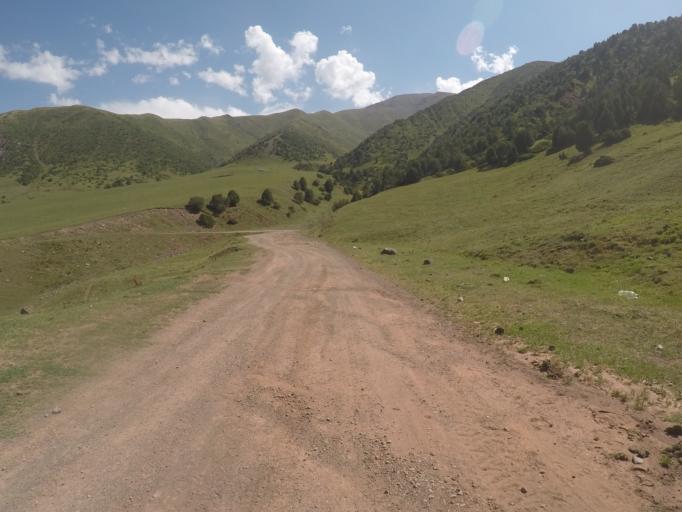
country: KG
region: Chuy
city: Bishkek
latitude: 42.6442
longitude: 74.5703
